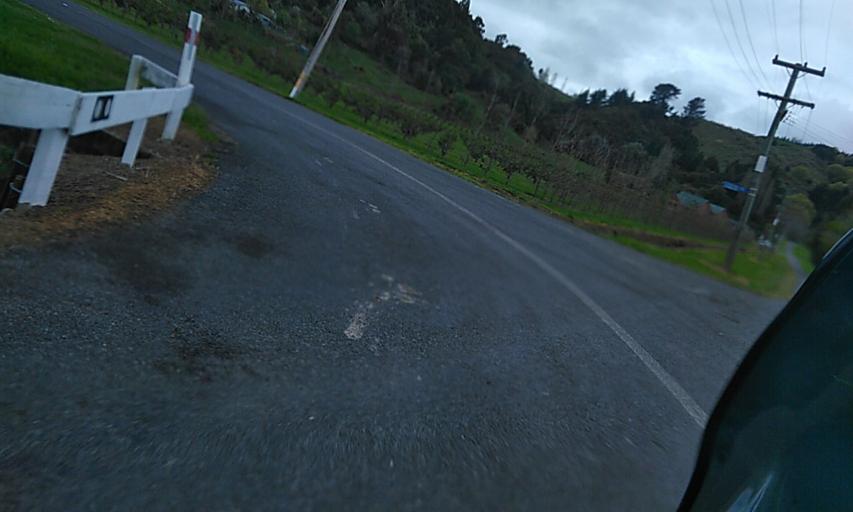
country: NZ
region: Gisborne
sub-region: Gisborne District
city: Gisborne
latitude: -38.5602
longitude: 177.9253
